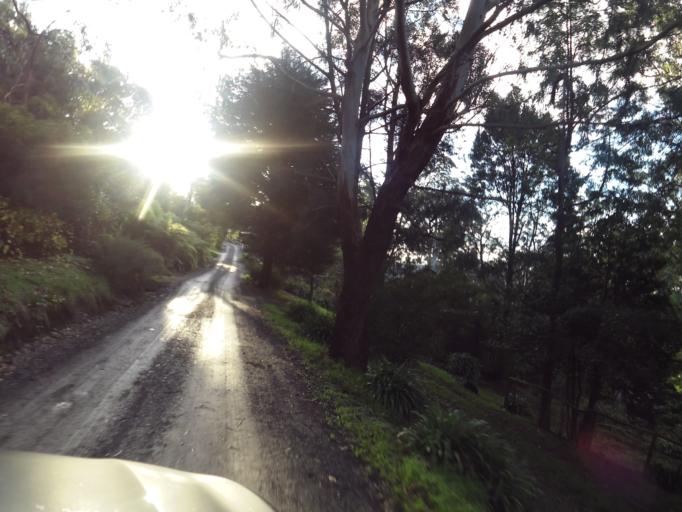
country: AU
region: Victoria
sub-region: Yarra Ranges
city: Ferny Creek
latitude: -37.8780
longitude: 145.3298
